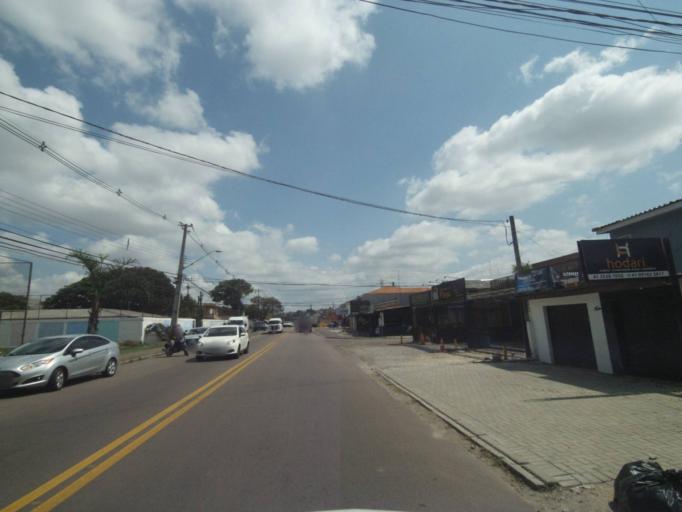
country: BR
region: Parana
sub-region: Sao Jose Dos Pinhais
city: Sao Jose dos Pinhais
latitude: -25.5340
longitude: -49.2577
